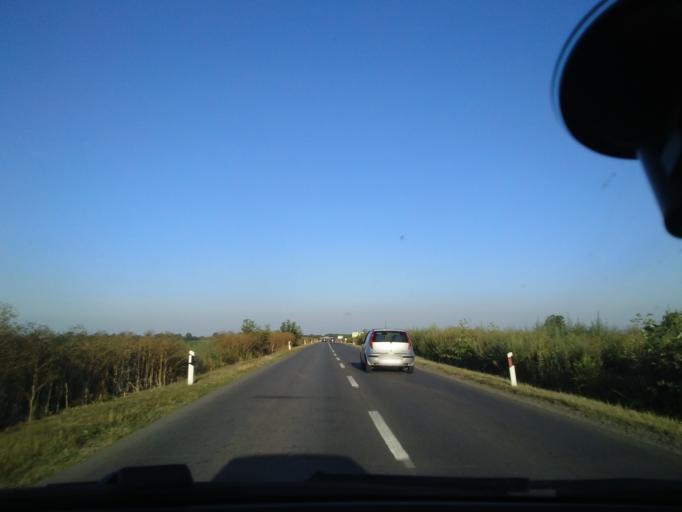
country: RS
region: Autonomna Pokrajina Vojvodina
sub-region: Juznobacki Okrug
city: Backi Petrovac
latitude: 45.3437
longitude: 19.6391
